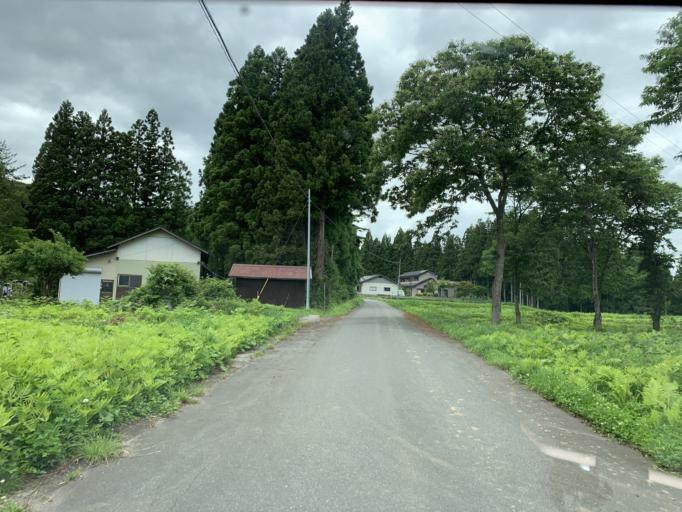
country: JP
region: Iwate
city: Ichinoseki
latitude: 38.9754
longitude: 140.9154
